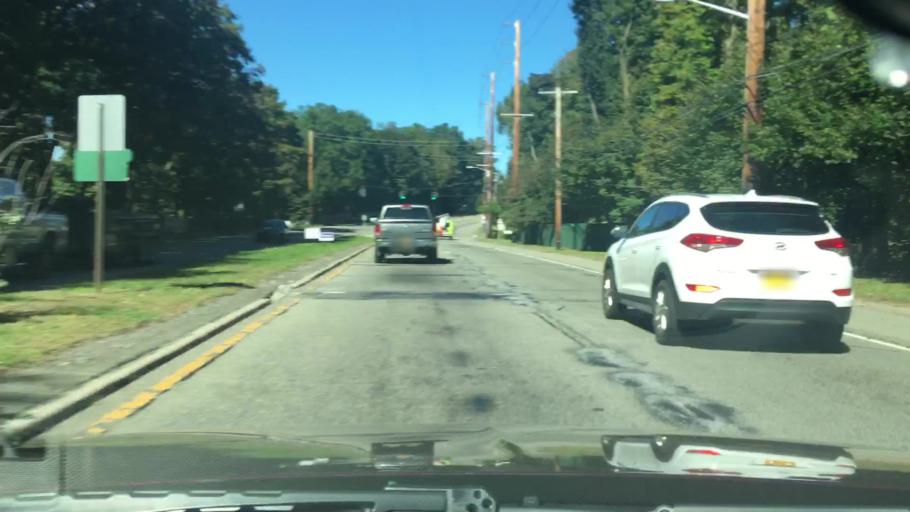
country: US
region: New York
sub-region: Nassau County
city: Flower Hill
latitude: 40.8125
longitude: -73.6791
